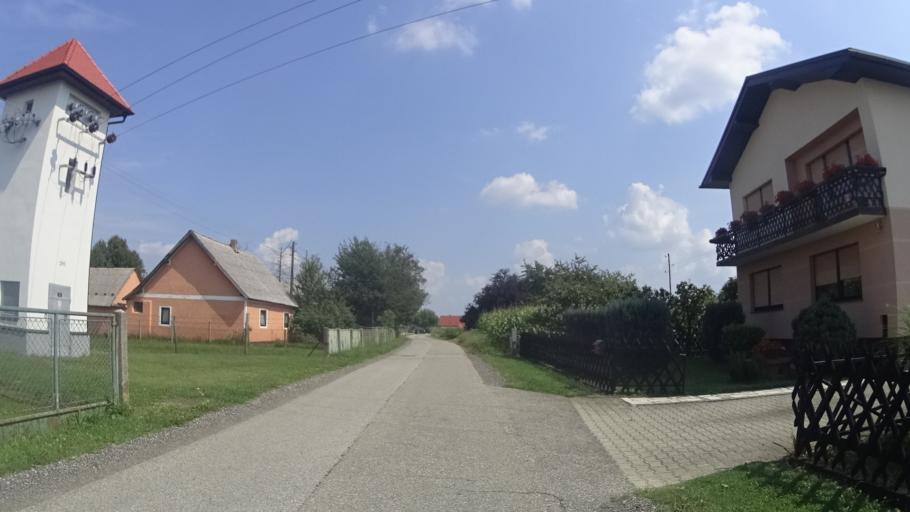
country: SI
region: Starse
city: Starse
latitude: 46.4497
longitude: 15.7401
